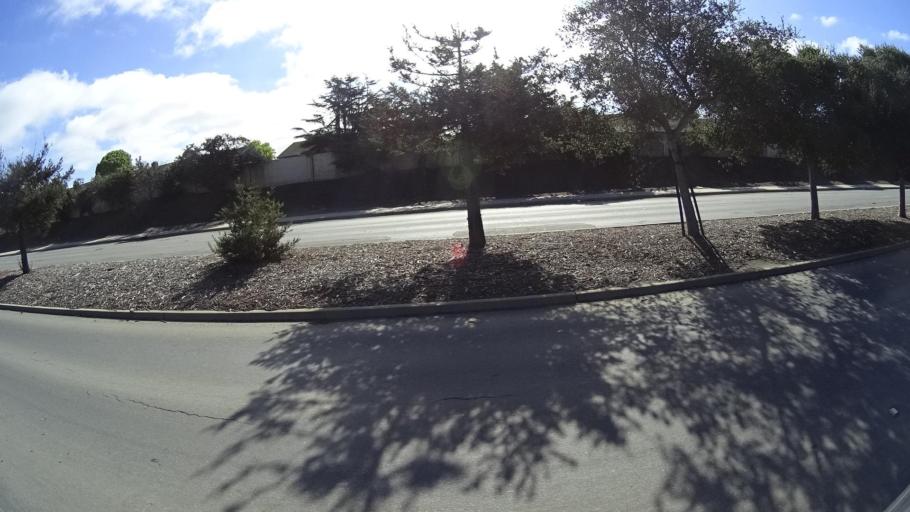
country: US
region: California
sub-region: Monterey County
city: Boronda
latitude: 36.6948
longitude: -121.6694
